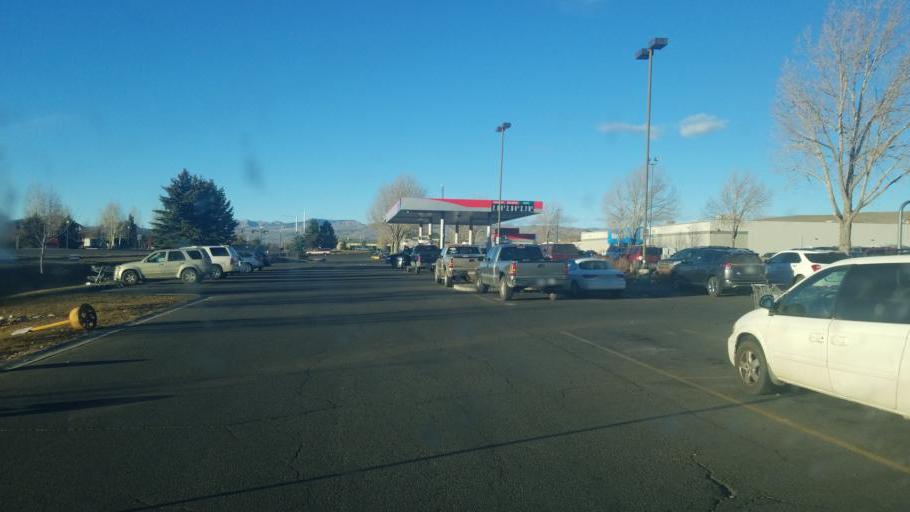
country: US
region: Colorado
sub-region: Gunnison County
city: Gunnison
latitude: 38.5531
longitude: -106.9265
